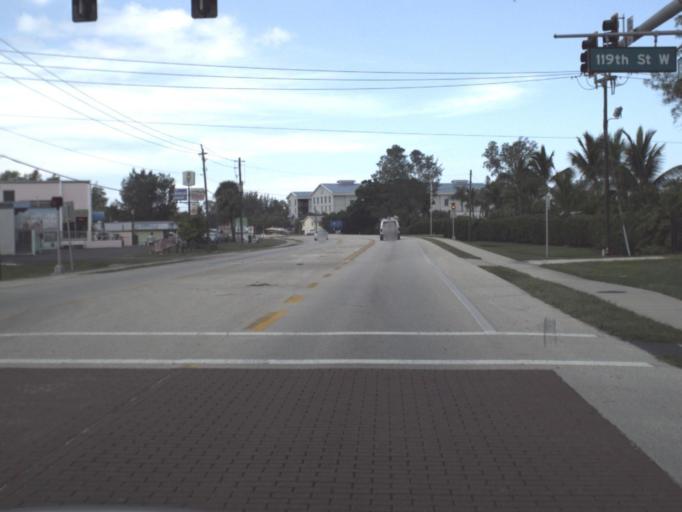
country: US
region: Florida
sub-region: Manatee County
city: Cortez
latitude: 27.4684
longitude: -82.6806
